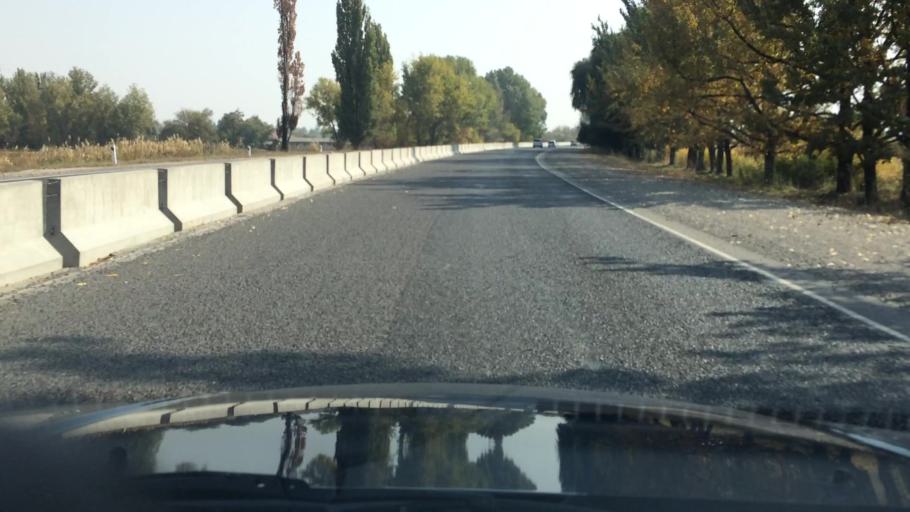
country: KG
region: Chuy
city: Kant
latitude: 42.9755
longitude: 74.8922
